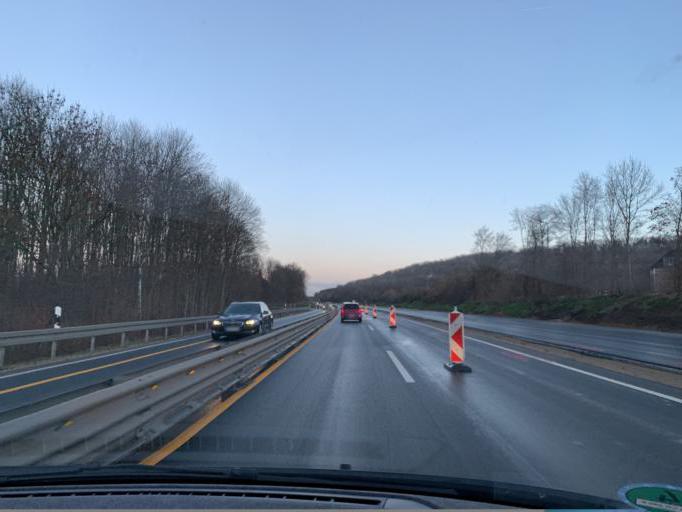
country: DE
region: North Rhine-Westphalia
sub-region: Regierungsbezirk Dusseldorf
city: Grevenbroich
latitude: 51.0759
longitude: 6.5938
